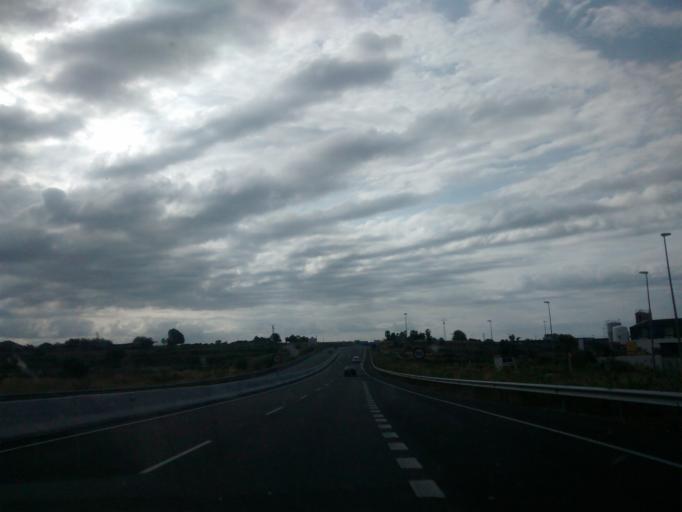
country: ES
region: Catalonia
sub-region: Provincia de Barcelona
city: Vilanova i la Geltru
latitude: 41.2405
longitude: 1.7302
